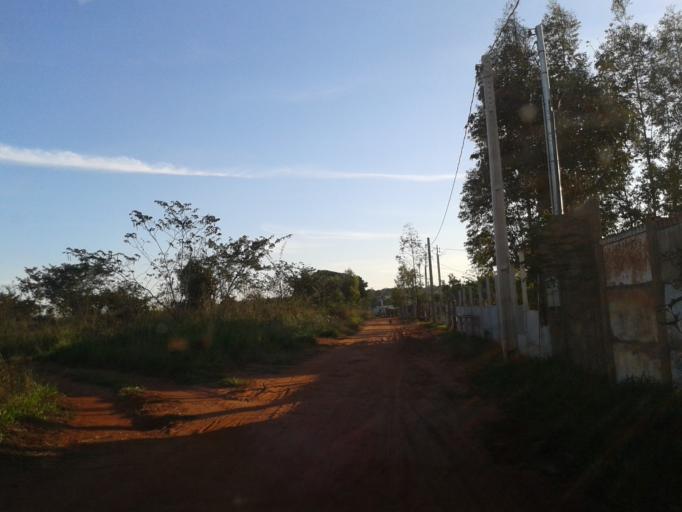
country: BR
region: Minas Gerais
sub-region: Santa Vitoria
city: Santa Vitoria
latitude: -19.0009
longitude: -50.3846
